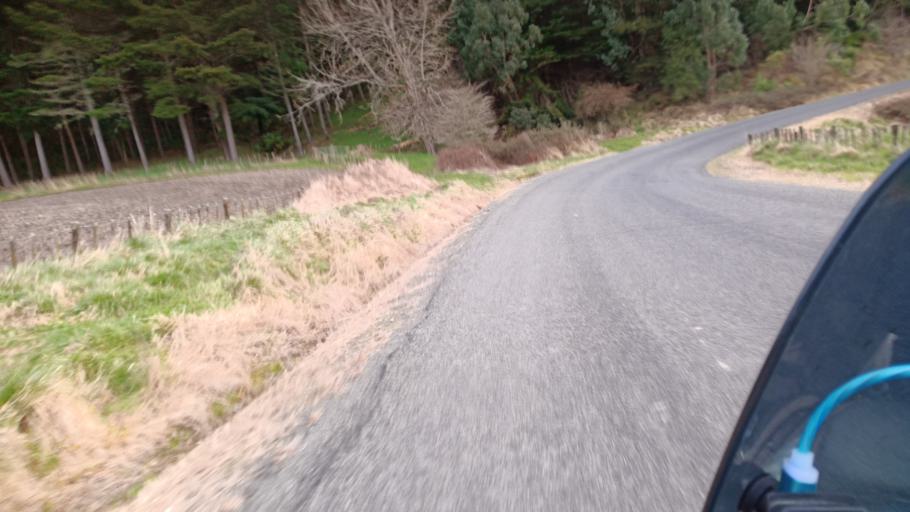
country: NZ
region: Hawke's Bay
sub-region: Wairoa District
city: Wairoa
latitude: -38.8182
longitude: 177.4718
